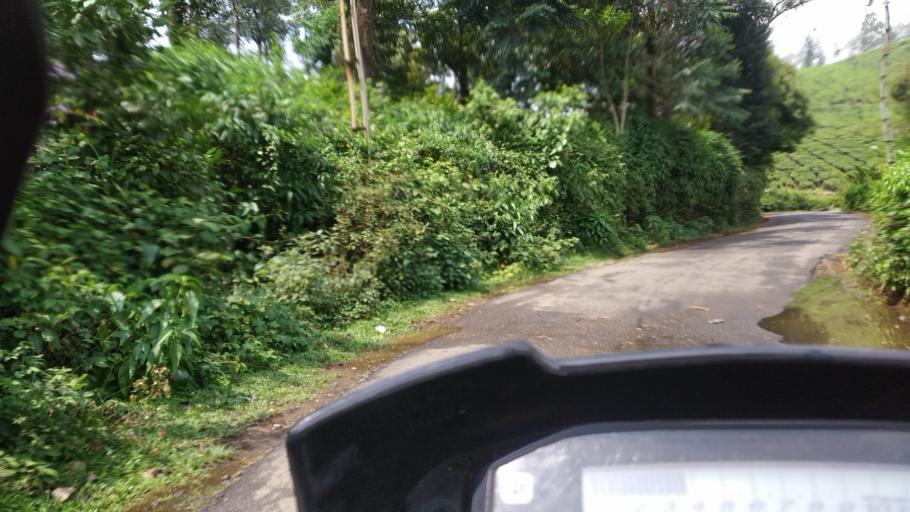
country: IN
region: Kerala
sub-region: Kottayam
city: Erattupetta
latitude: 9.6287
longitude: 76.9654
